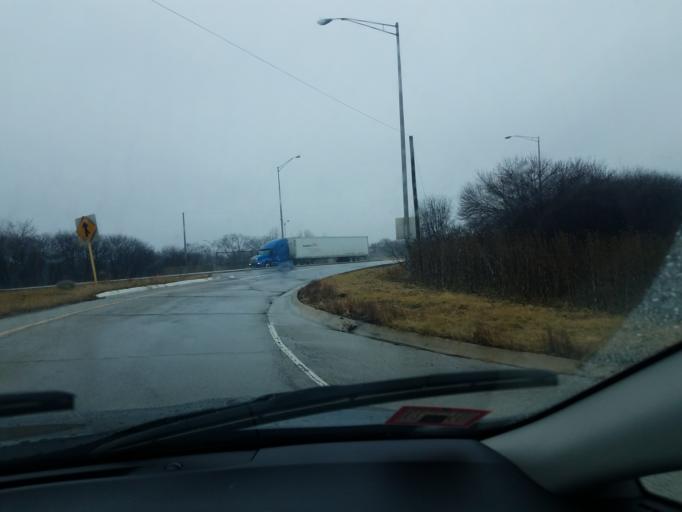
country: US
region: Illinois
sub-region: Cook County
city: Lincolnwood
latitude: 42.0121
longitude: -87.7495
